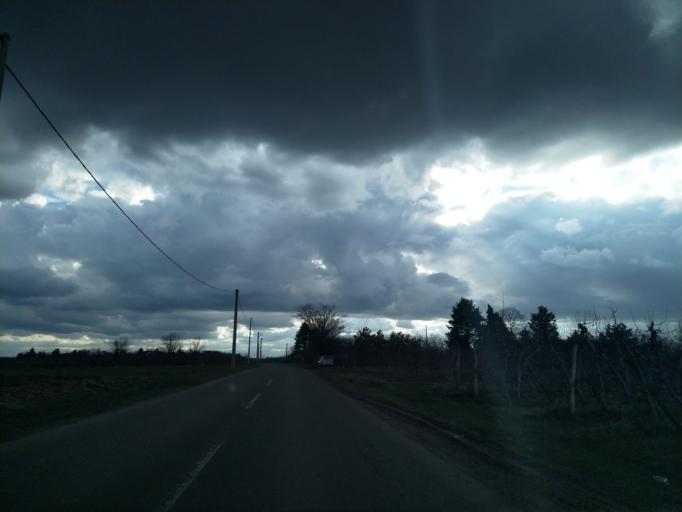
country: RS
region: Central Serbia
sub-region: Belgrade
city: Grocka
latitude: 44.6287
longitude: 20.7456
